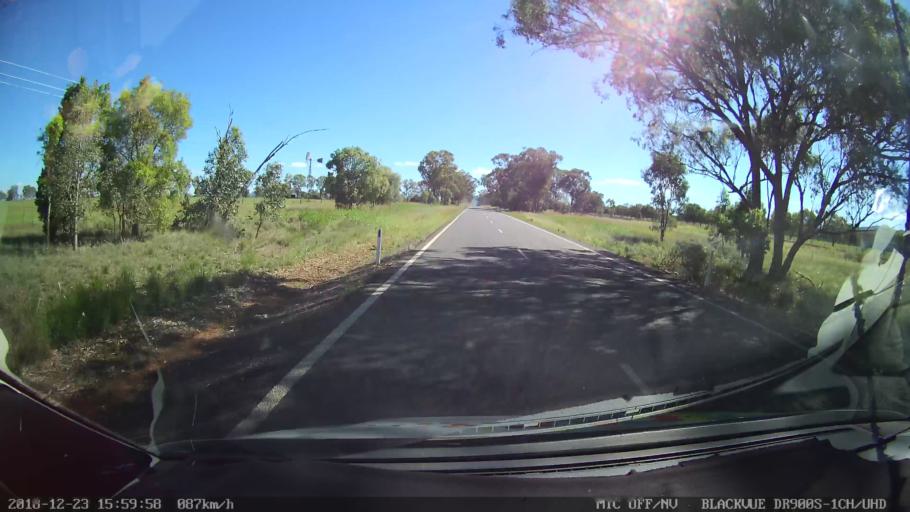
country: AU
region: New South Wales
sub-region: Tamworth Municipality
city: Phillip
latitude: -31.2055
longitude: 150.8289
